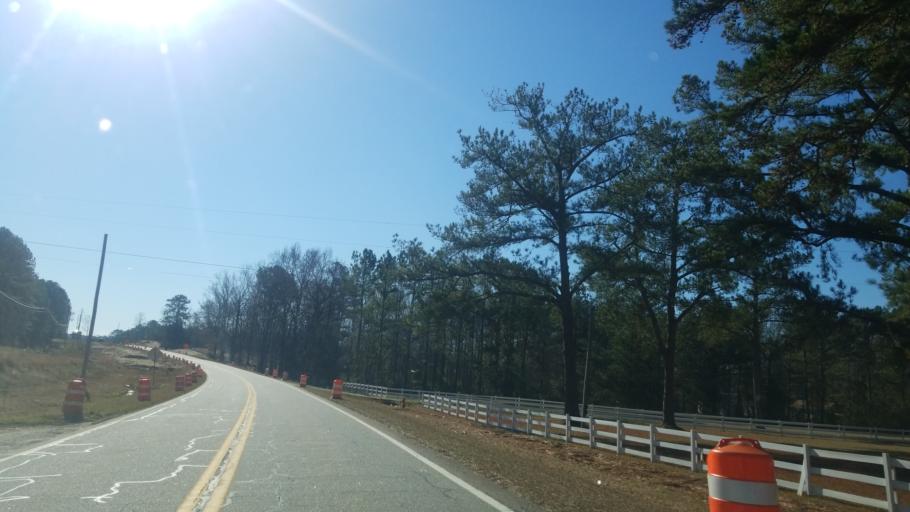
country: US
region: Alabama
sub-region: Lee County
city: Smiths Station
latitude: 32.6605
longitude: -85.0601
